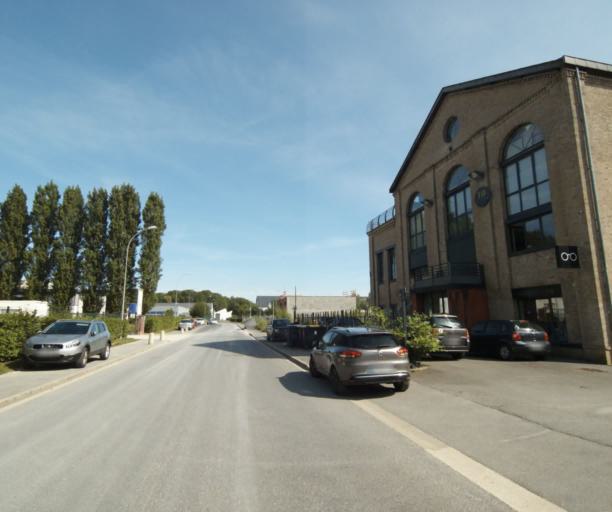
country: FR
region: Champagne-Ardenne
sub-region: Departement des Ardennes
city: Villers-Semeuse
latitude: 49.7407
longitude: 4.7295
